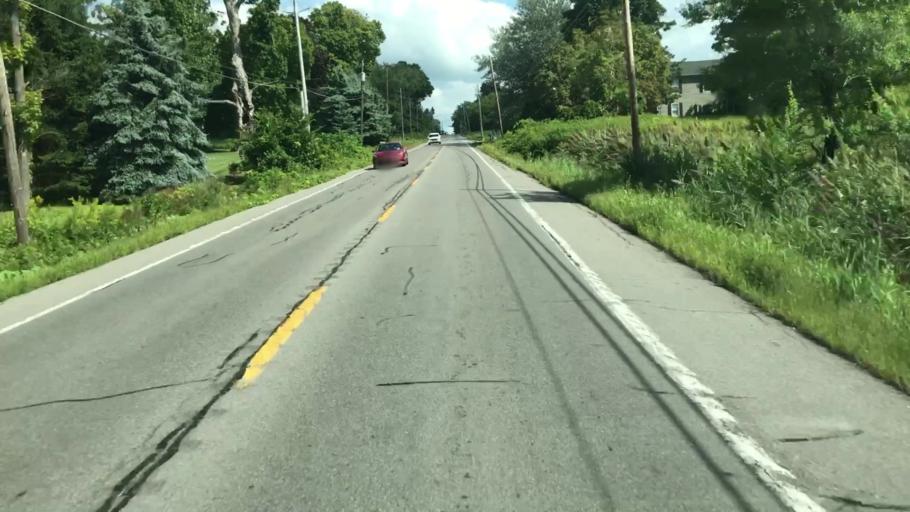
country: US
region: New York
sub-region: Onondaga County
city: Marcellus
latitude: 42.9835
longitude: -76.3159
